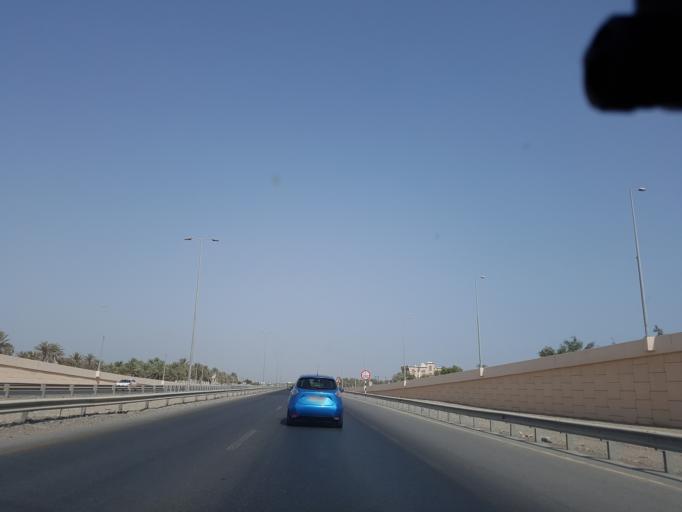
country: OM
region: Al Batinah
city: Barka'
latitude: 23.7204
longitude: 57.7375
